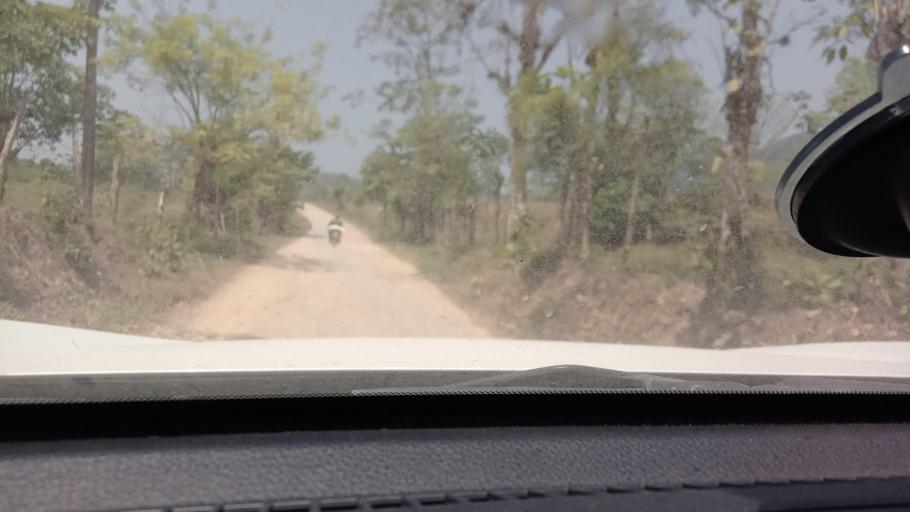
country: MX
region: Tabasco
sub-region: Huimanguillo
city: Francisco Rueda
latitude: 17.5157
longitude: -93.8914
